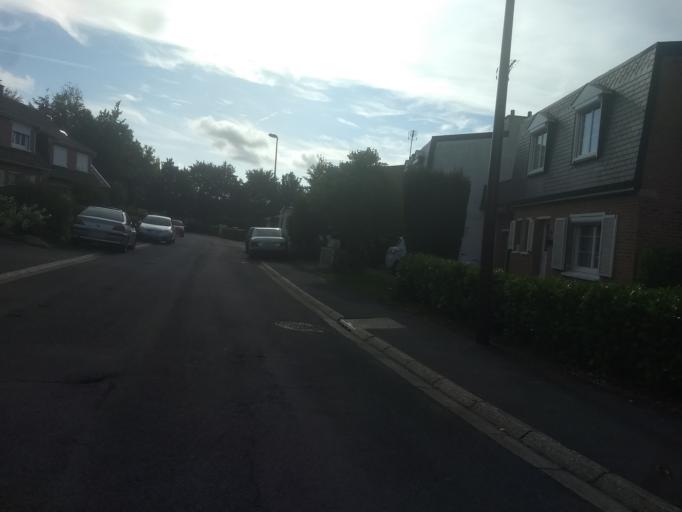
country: FR
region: Nord-Pas-de-Calais
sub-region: Departement du Pas-de-Calais
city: Dainville
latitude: 50.2848
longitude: 2.7323
